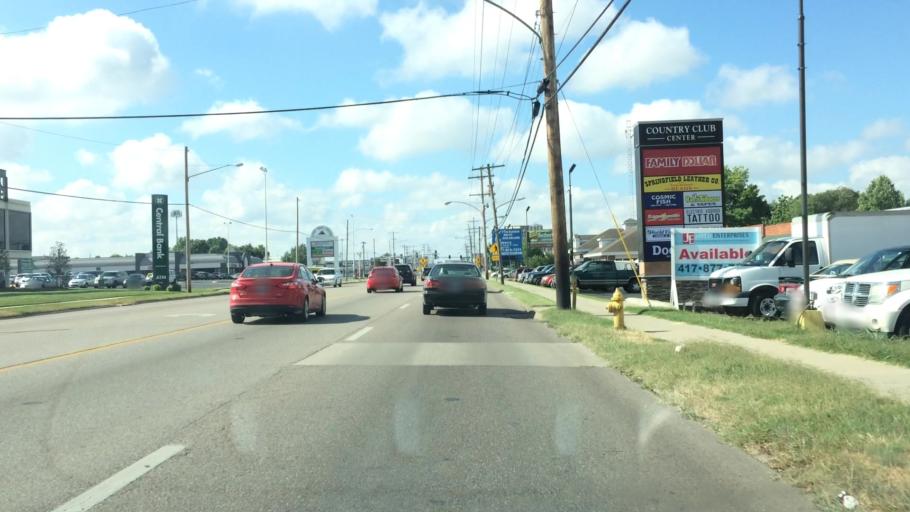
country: US
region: Missouri
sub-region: Greene County
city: Springfield
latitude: 37.1882
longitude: -93.2623
